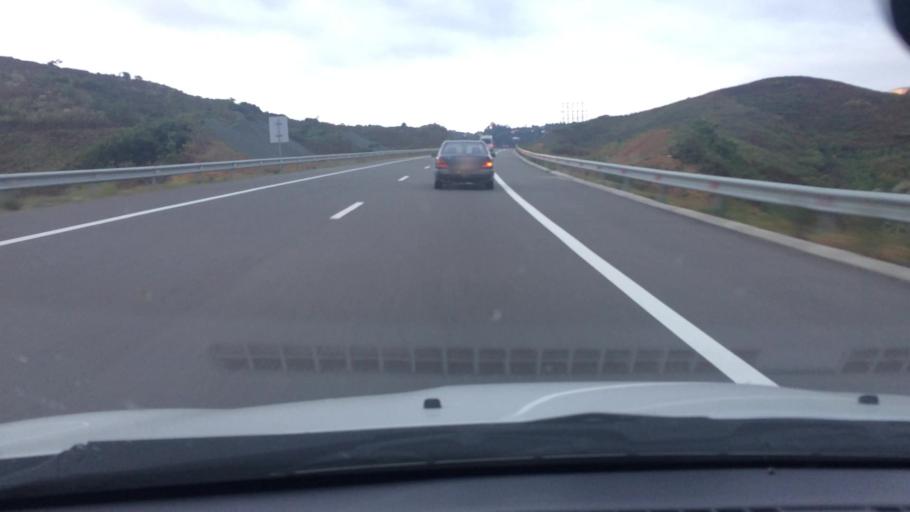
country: GE
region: Ajaria
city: Makhinjauri
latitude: 41.7258
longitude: 41.7498
